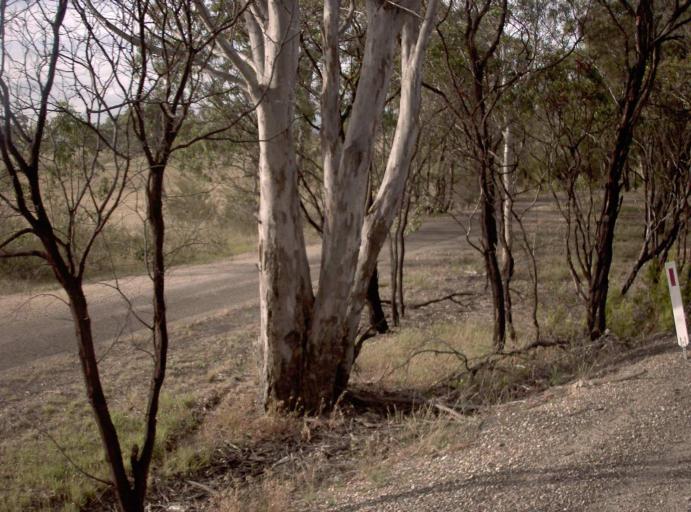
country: AU
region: Victoria
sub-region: Wellington
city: Sale
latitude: -37.9273
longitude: 146.9925
